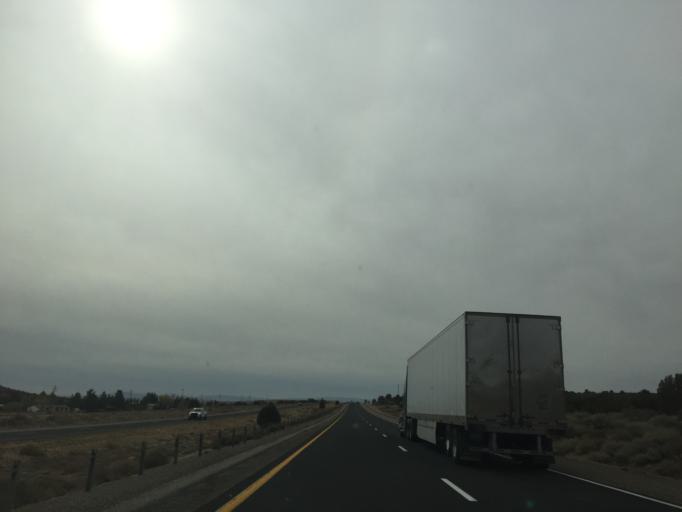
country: US
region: Utah
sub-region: Washington County
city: Toquerville
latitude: 37.2646
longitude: -113.3255
